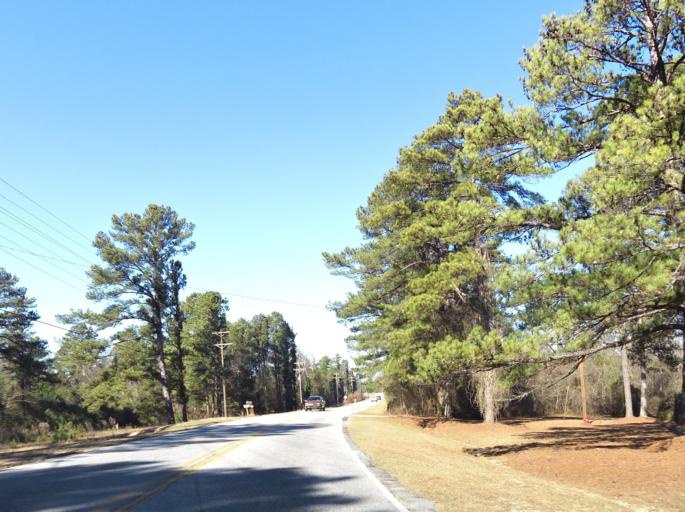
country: US
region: Georgia
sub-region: Bibb County
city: West Point
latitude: 32.7508
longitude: -83.7420
